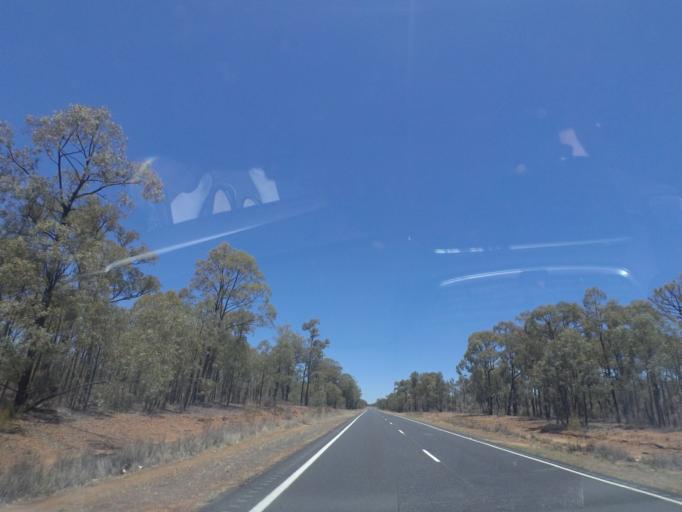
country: AU
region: New South Wales
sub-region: Warrumbungle Shire
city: Coonabarabran
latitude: -30.8634
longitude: 149.4531
